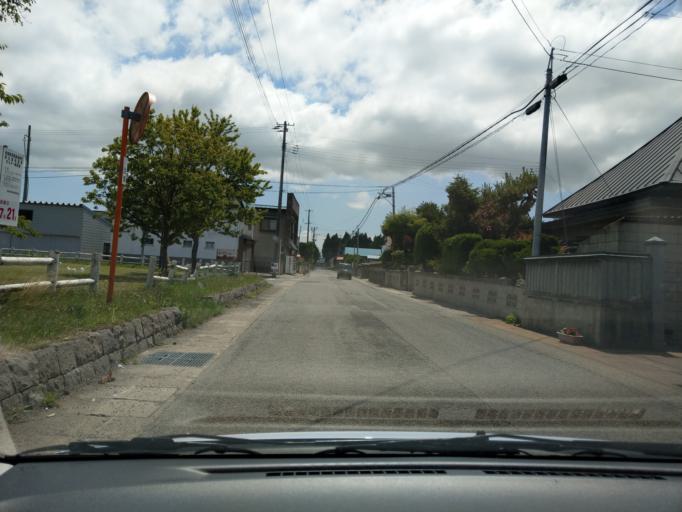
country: JP
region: Aomori
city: Kuroishi
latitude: 40.6802
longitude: 140.5599
